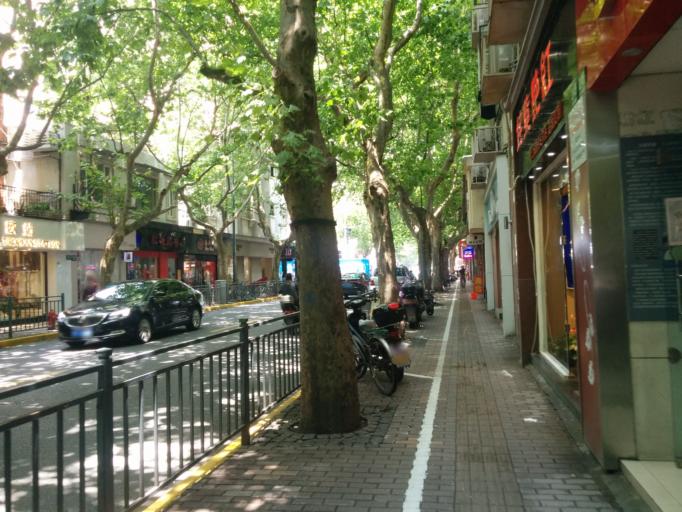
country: CN
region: Shanghai Shi
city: Shanghai
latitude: 31.2185
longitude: 121.4571
